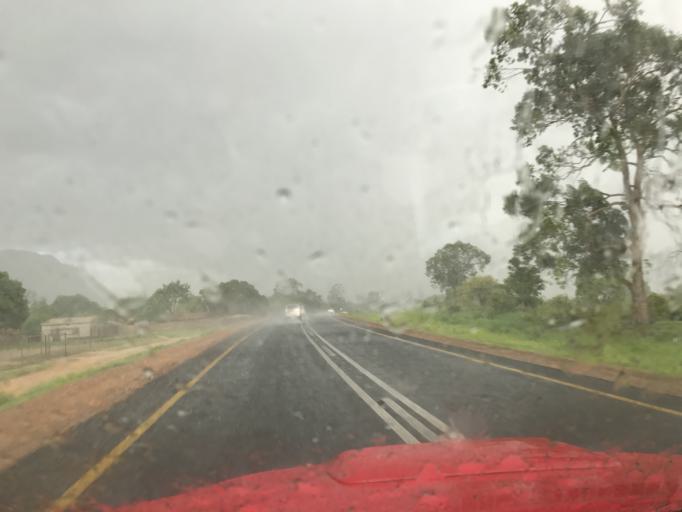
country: MZ
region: Nampula
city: Nampula
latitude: -15.0027
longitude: 38.5104
